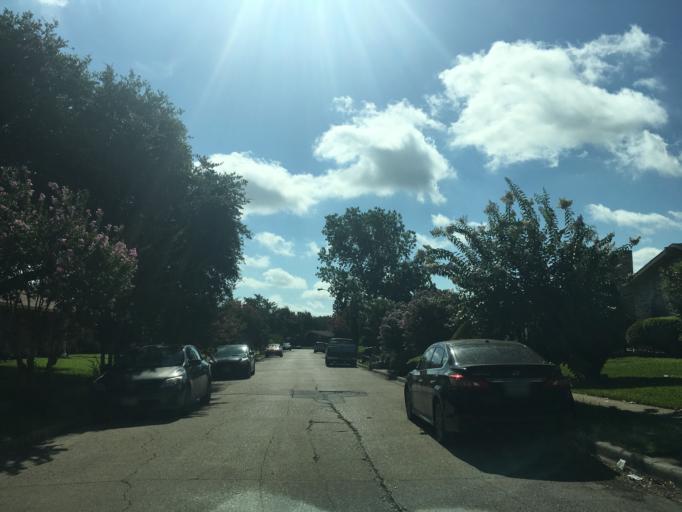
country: US
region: Texas
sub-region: Dallas County
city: Garland
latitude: 32.8515
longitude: -96.6616
